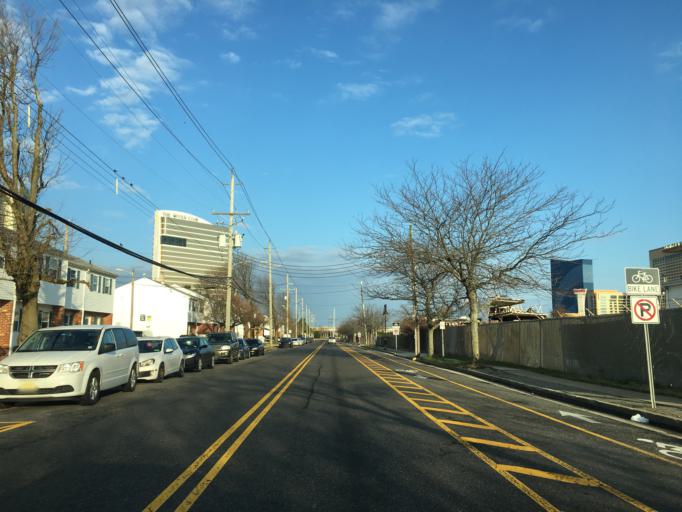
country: US
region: New Jersey
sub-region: Atlantic County
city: Atlantic City
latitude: 39.3742
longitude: -74.4283
